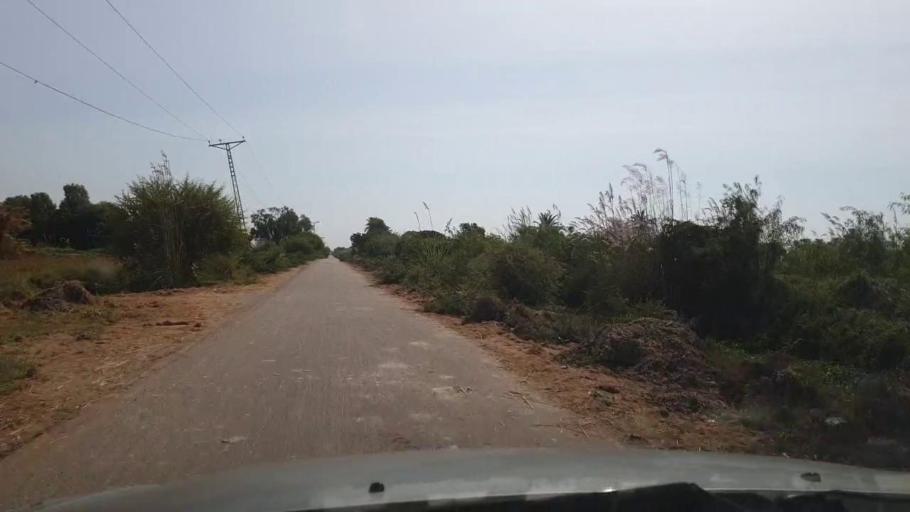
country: PK
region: Sindh
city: Tando Muhammad Khan
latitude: 25.1542
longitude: 68.3832
